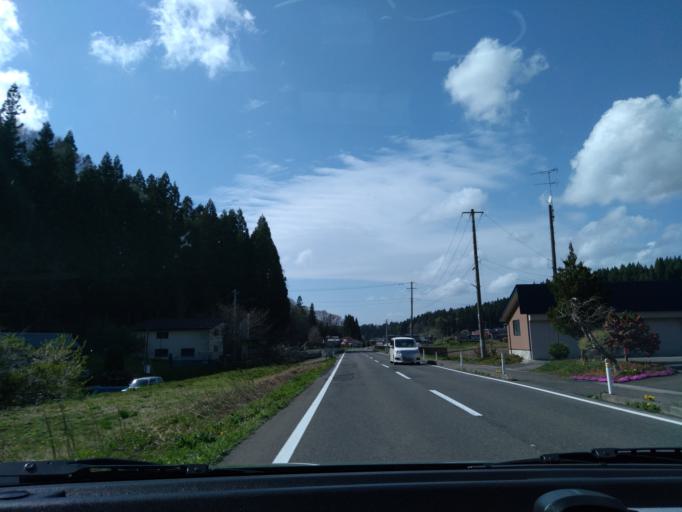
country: JP
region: Akita
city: Akita
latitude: 39.7076
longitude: 140.2070
